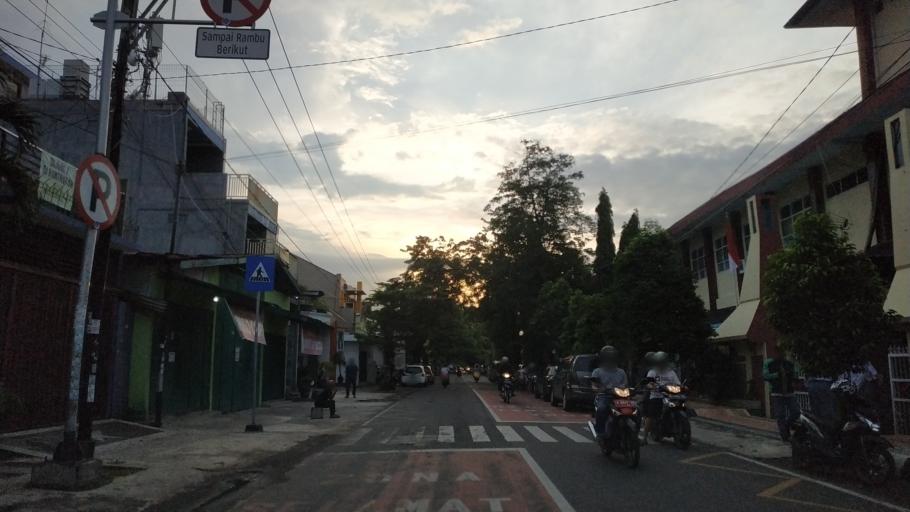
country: ID
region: Central Java
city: Kudus
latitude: -6.8118
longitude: 110.8516
